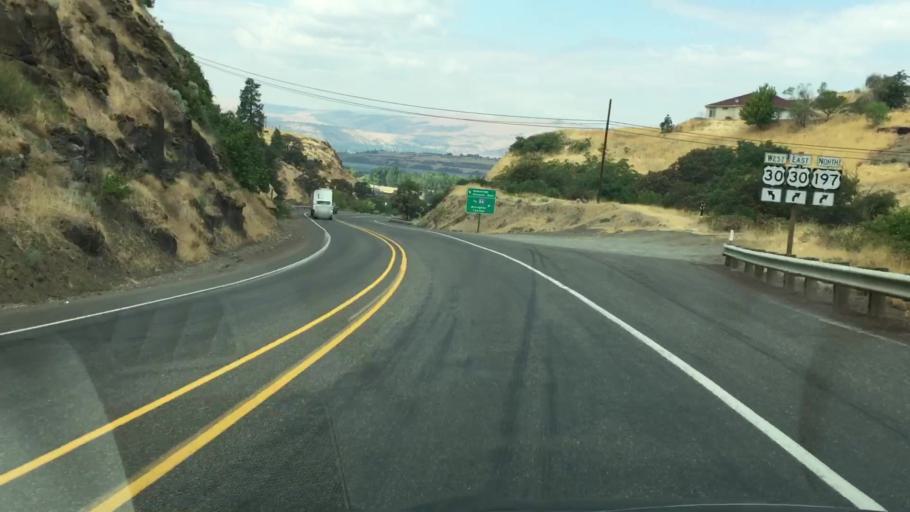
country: US
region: Oregon
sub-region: Wasco County
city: The Dalles
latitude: 45.5975
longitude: -121.1363
